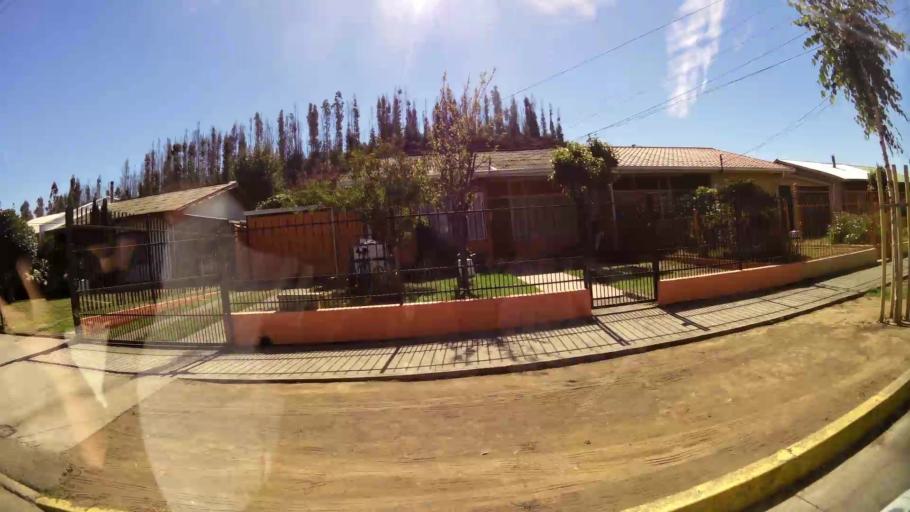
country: CL
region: Biobio
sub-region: Provincia de Concepcion
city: Penco
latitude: -36.7508
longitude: -72.9989
